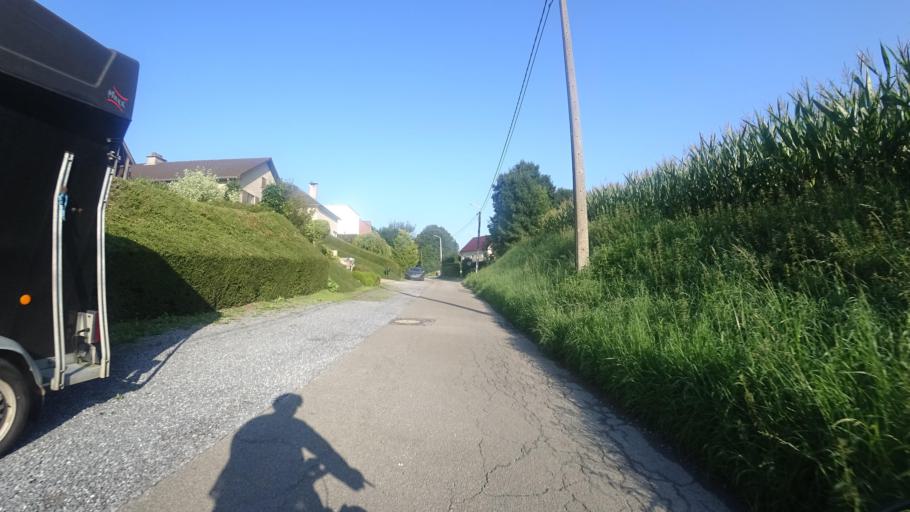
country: BE
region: Flanders
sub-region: Provincie Vlaams-Brabant
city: Overijse
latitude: 50.7781
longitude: 4.5316
